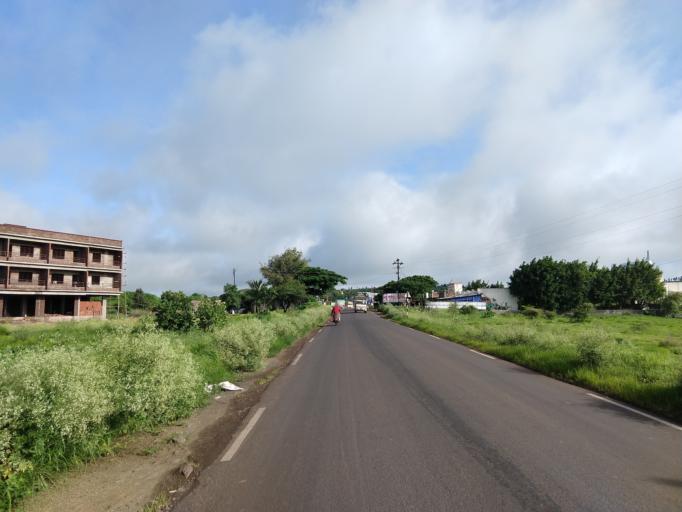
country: IN
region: Maharashtra
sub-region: Pune Division
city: Khed
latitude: 18.3953
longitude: 73.9157
